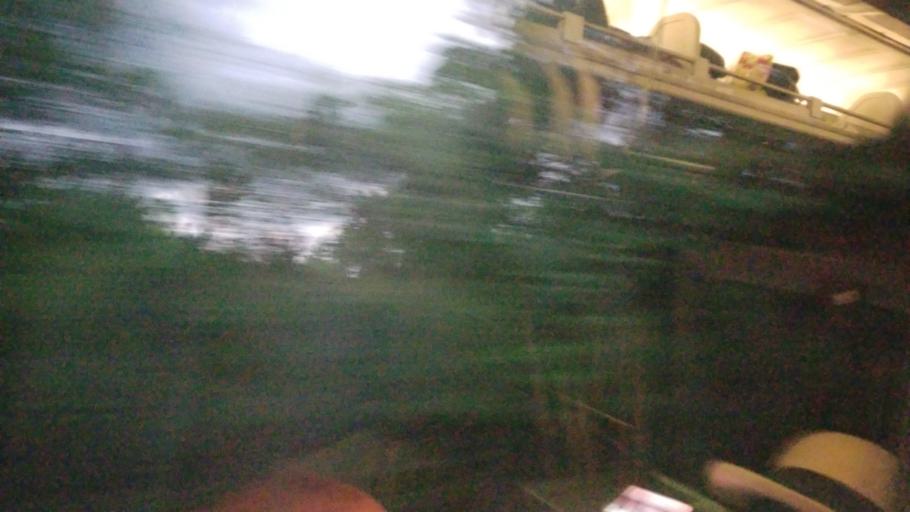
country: US
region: Virginia
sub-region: Orange County
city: Gordonsville
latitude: 38.1818
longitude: -78.2593
